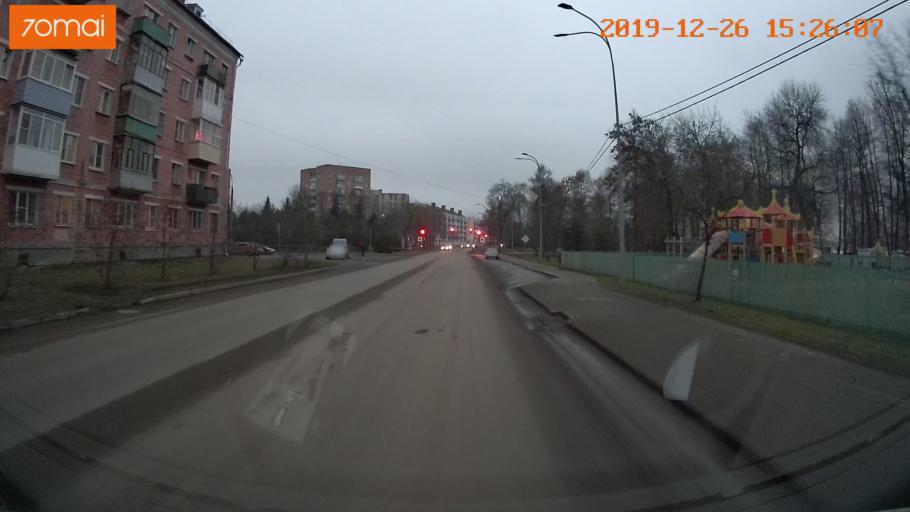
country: RU
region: Jaroslavl
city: Rybinsk
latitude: 58.0560
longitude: 38.8310
